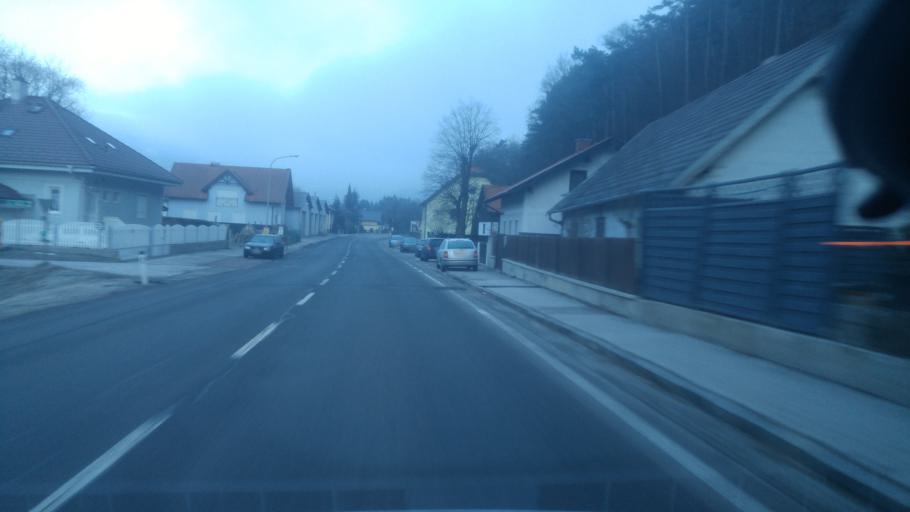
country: AT
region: Lower Austria
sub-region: Politischer Bezirk Baden
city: Pottenstein
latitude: 47.9715
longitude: 16.0745
